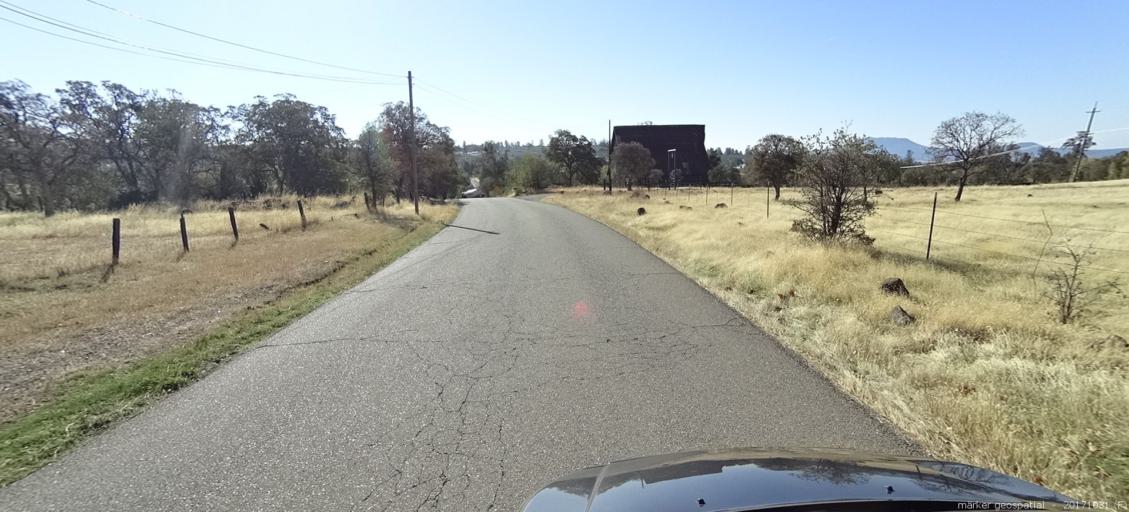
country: US
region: California
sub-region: Shasta County
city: Shingletown
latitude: 40.4396
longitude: -121.8713
